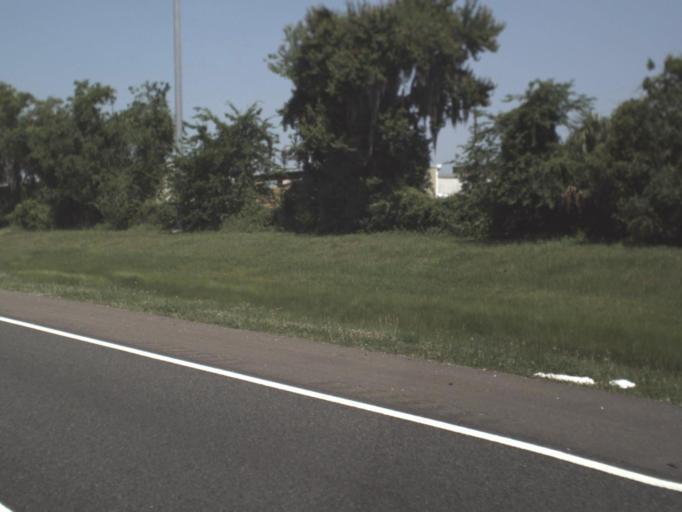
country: US
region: Florida
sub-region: Duval County
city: Baldwin
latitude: 30.3079
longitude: -81.8665
